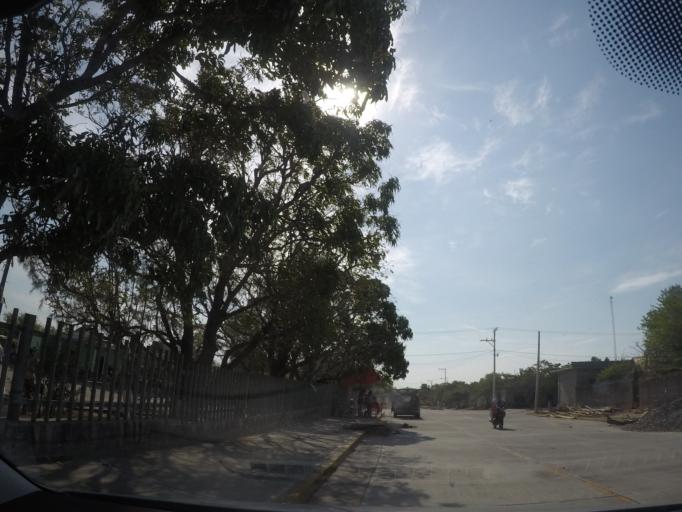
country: MX
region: Oaxaca
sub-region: Salina Cruz
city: Salina Cruz
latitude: 16.2197
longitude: -95.1276
